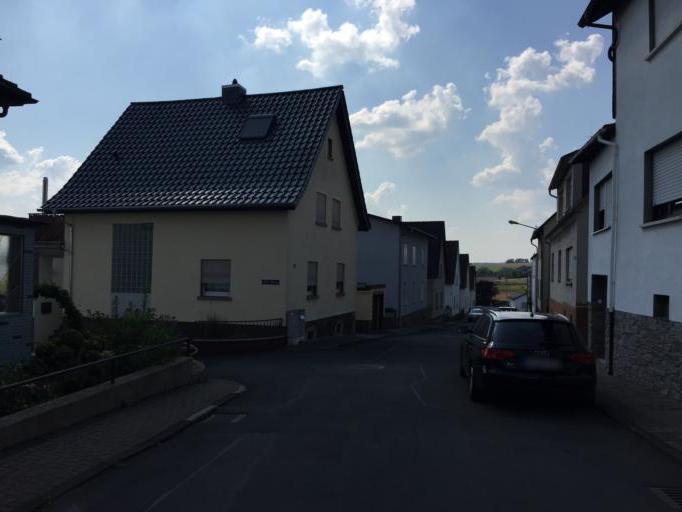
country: DE
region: Hesse
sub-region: Regierungsbezirk Giessen
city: Heuchelheim
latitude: 50.6267
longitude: 8.6322
